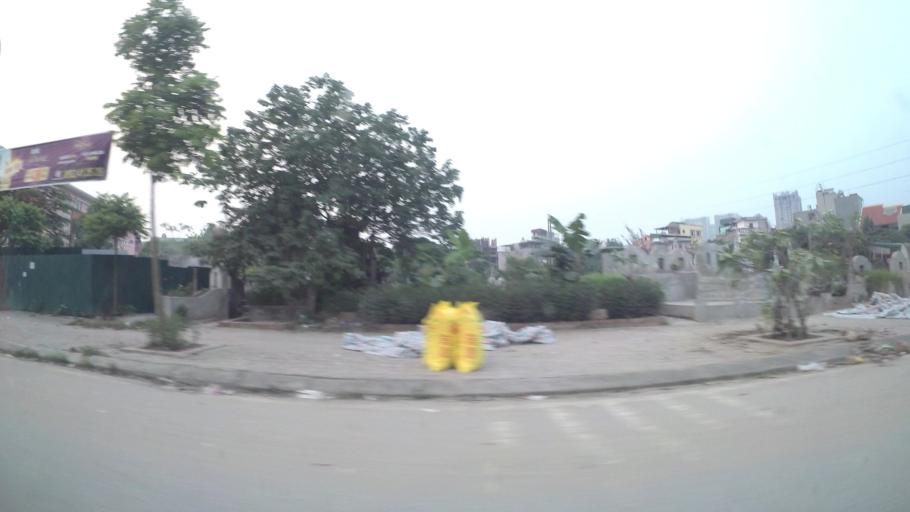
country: VN
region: Ha Noi
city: Thanh Xuan
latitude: 20.9772
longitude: 105.8024
